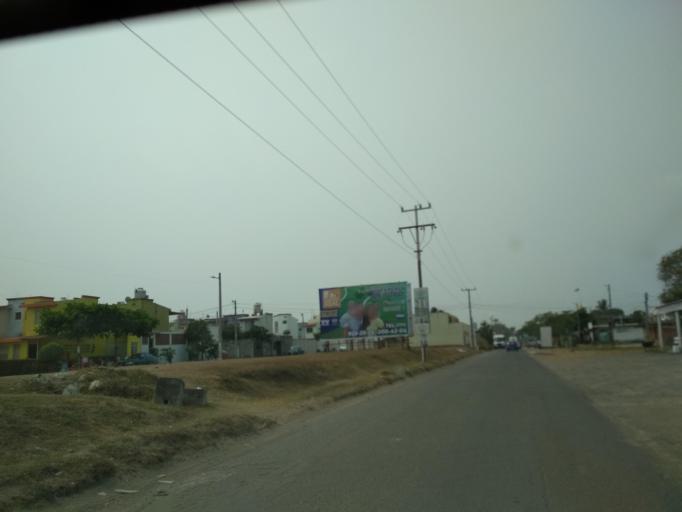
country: MX
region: Veracruz
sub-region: Veracruz
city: Las Amapolas
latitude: 19.1594
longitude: -96.2215
